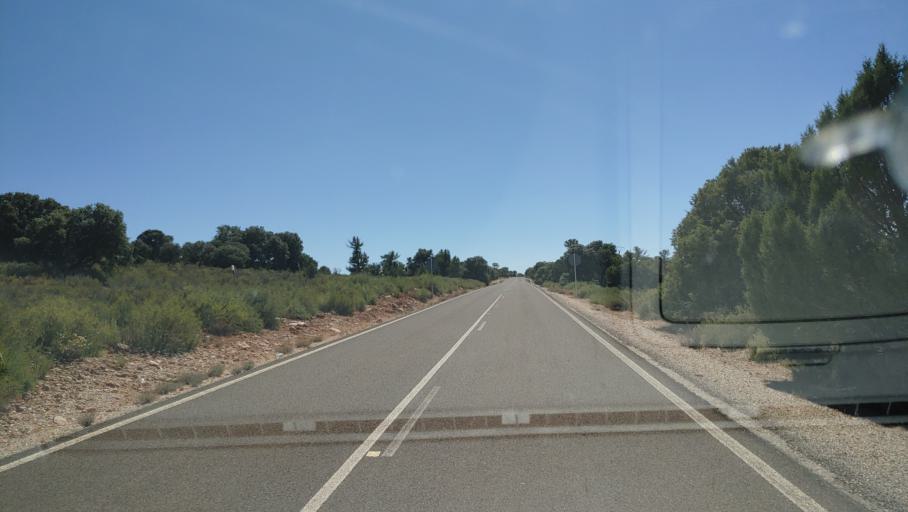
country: ES
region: Castille-La Mancha
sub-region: Provincia de Ciudad Real
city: Villahermosa
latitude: 38.8491
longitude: -2.8073
